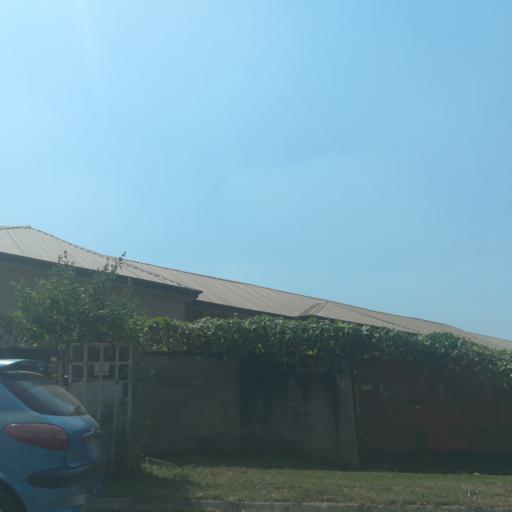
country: NG
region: Abuja Federal Capital Territory
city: Abuja
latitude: 9.0686
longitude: 7.4484
